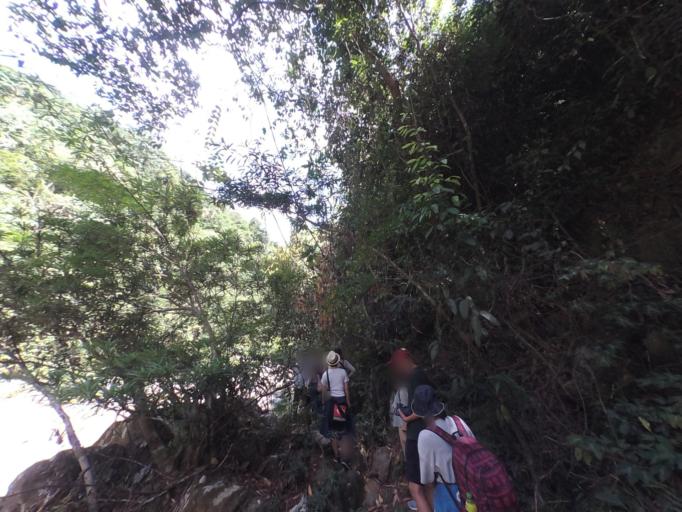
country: VN
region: Thua Thien-Hue
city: A Luoi
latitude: 16.3068
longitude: 107.3239
